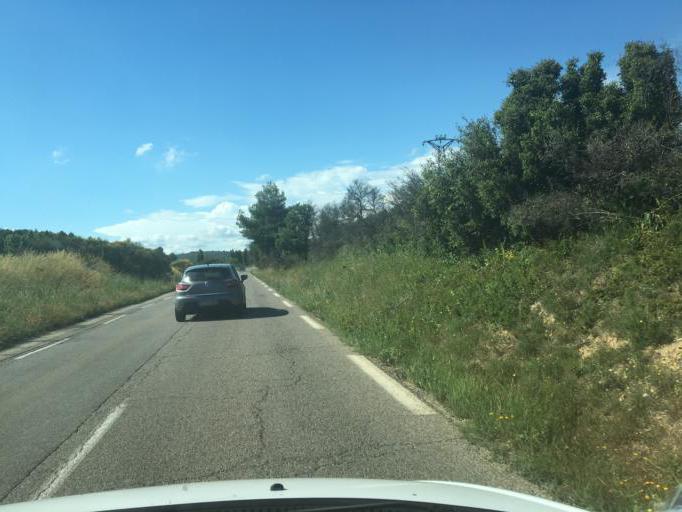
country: FR
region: Provence-Alpes-Cote d'Azur
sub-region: Departement des Bouches-du-Rhone
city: Eguilles
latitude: 43.5324
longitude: 5.3501
